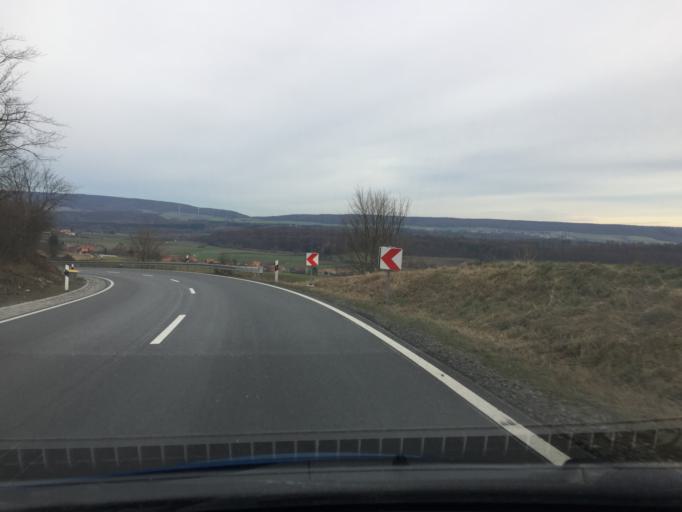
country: DE
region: Lower Saxony
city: Luerdissen
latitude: 51.9704
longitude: 9.6522
